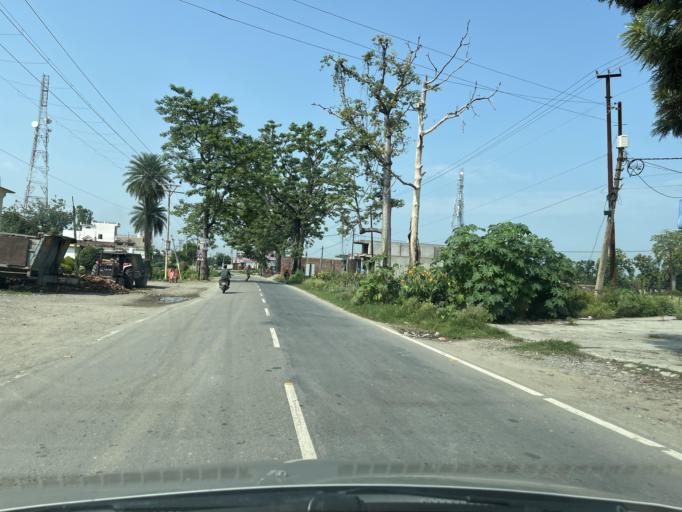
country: IN
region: Uttarakhand
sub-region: Udham Singh Nagar
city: Bazpur
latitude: 29.2103
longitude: 79.2159
